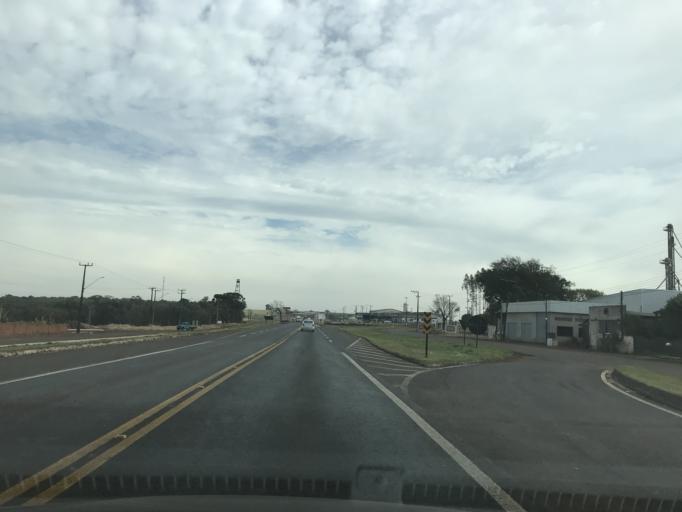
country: BR
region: Parana
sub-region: Cascavel
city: Cascavel
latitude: -25.0518
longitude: -53.6289
